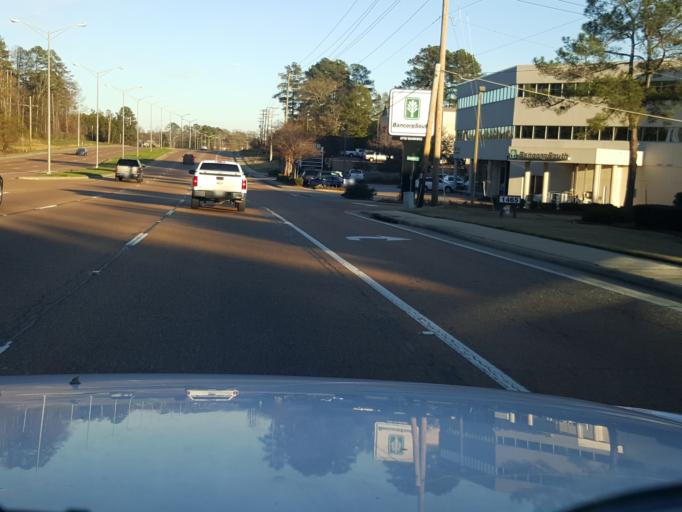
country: US
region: Mississippi
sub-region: Rankin County
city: Flowood
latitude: 32.3340
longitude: -90.1487
